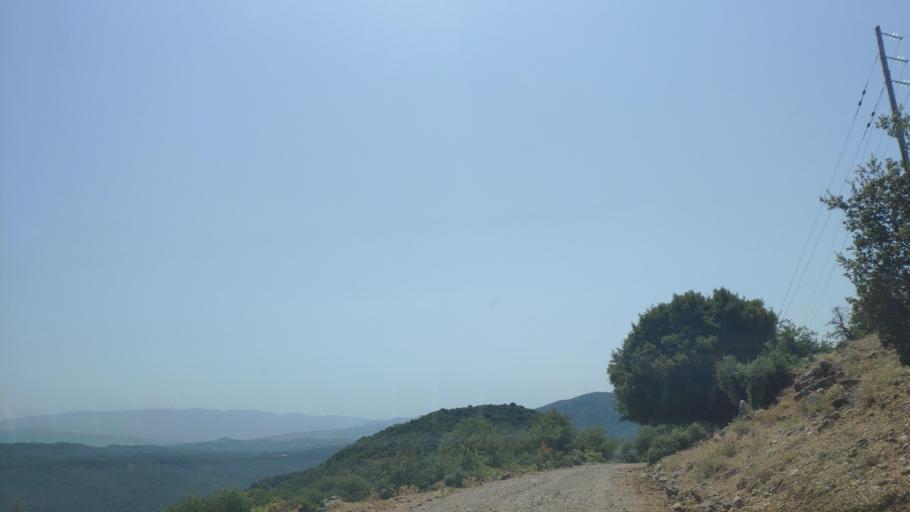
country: GR
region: West Greece
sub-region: Nomos Aitolias kai Akarnanias
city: Monastirakion
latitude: 38.8161
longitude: 21.0249
